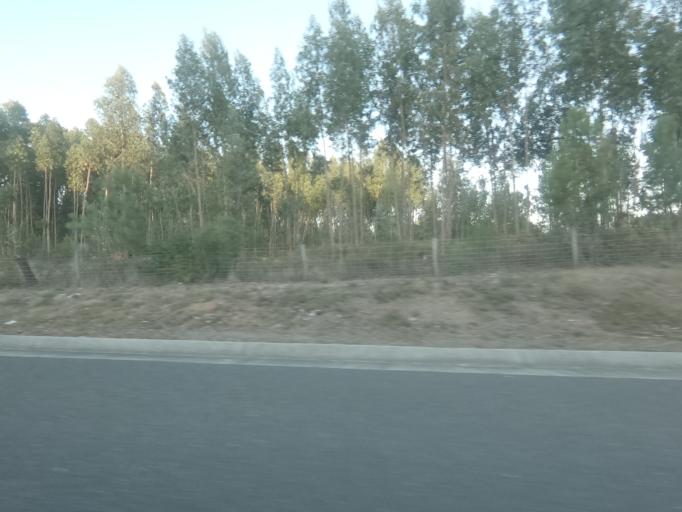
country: PT
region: Leiria
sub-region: Leiria
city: Santa Catarina da Serra
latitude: 39.6537
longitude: -8.6961
